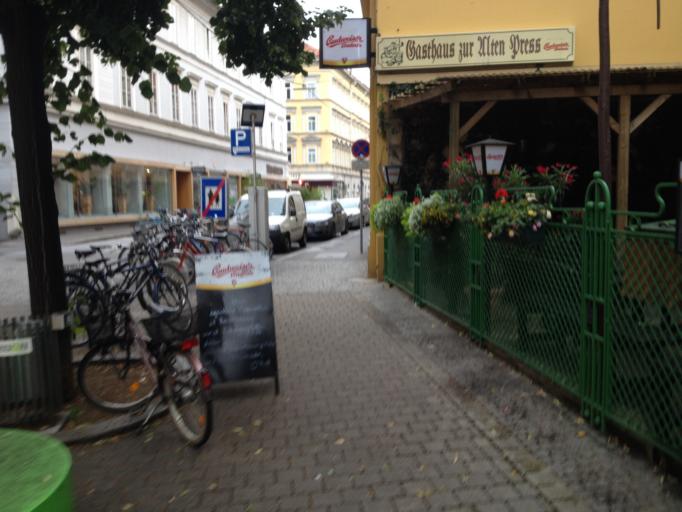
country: AT
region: Styria
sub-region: Graz Stadt
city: Graz
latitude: 47.0700
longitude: 15.4333
